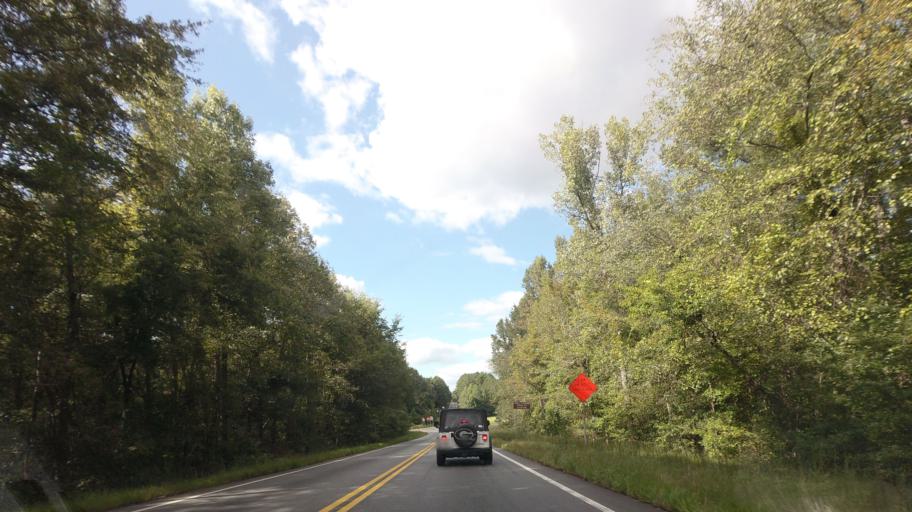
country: US
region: Georgia
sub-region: Monroe County
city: Forsyth
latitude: 33.0227
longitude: -83.7447
